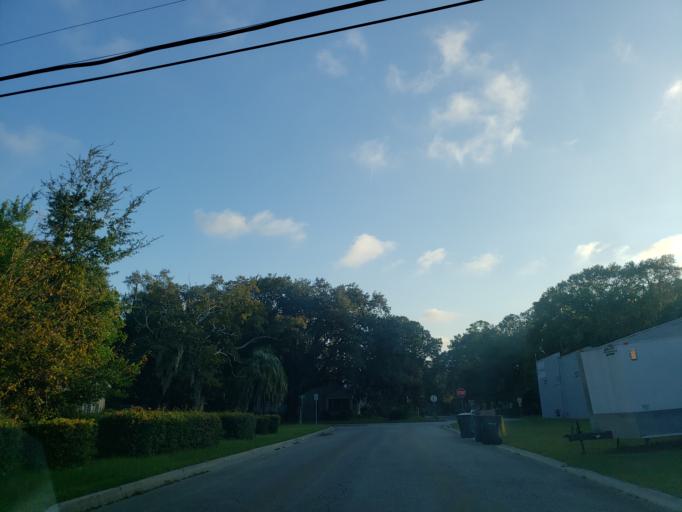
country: US
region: Georgia
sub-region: Chatham County
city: Thunderbolt
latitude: 32.0497
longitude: -81.0740
